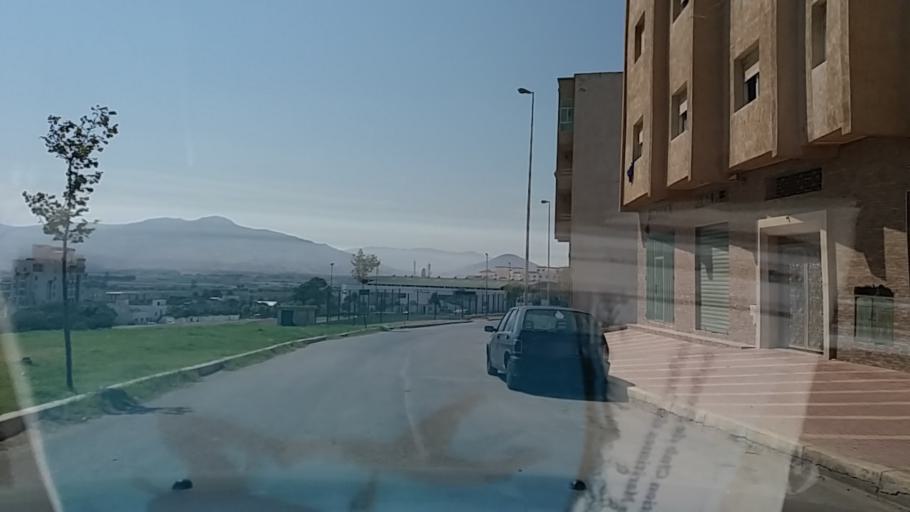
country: MA
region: Tanger-Tetouan
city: Tetouan
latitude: 35.5675
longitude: -5.4093
